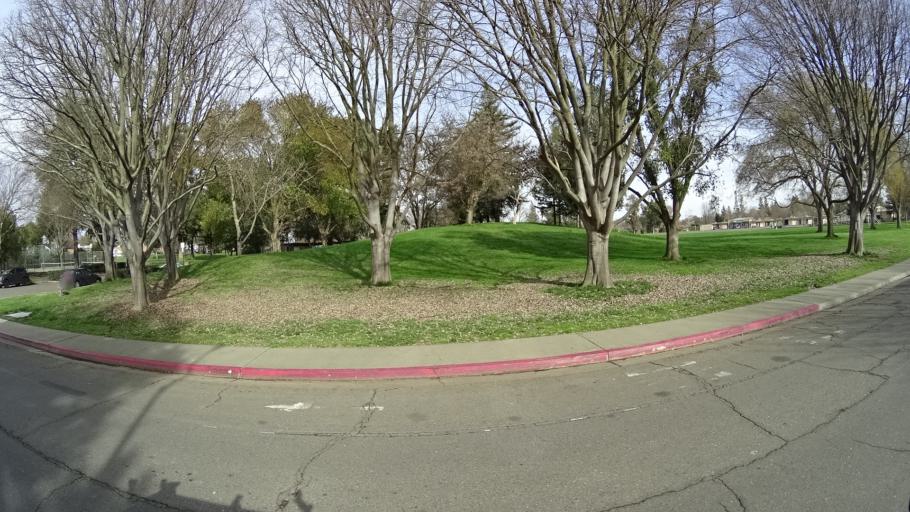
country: US
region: California
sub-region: Yolo County
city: Davis
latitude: 38.5506
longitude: -121.6884
